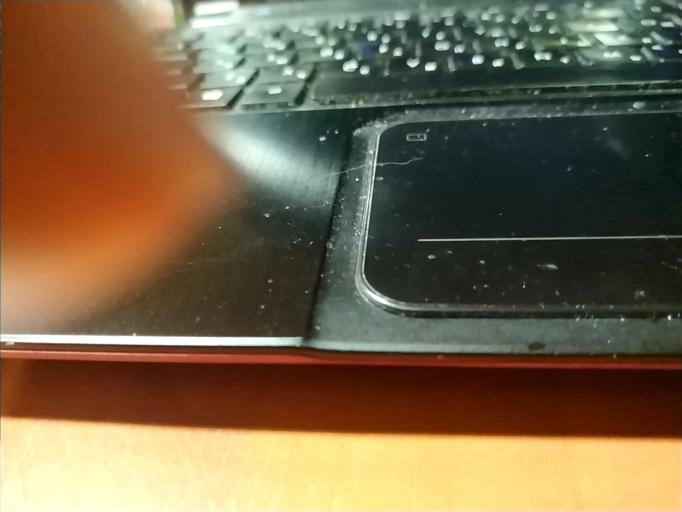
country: RU
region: Tverskaya
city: Ves'yegonsk
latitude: 58.7051
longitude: 37.5439
